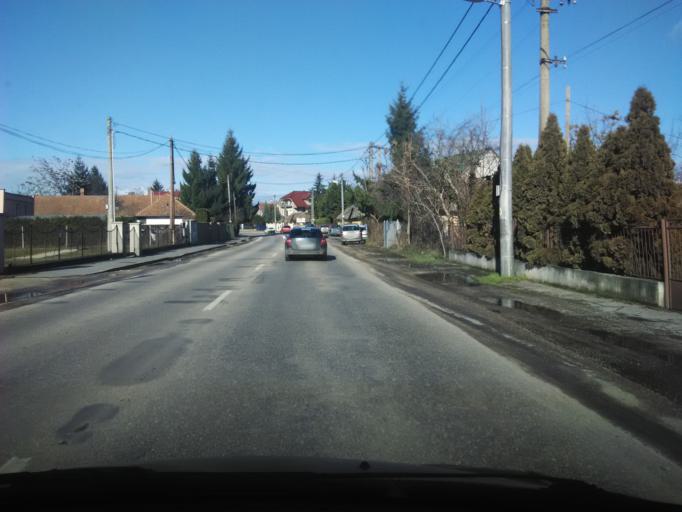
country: SK
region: Nitriansky
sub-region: Okres Nitra
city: Nitra
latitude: 48.2368
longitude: 18.1231
